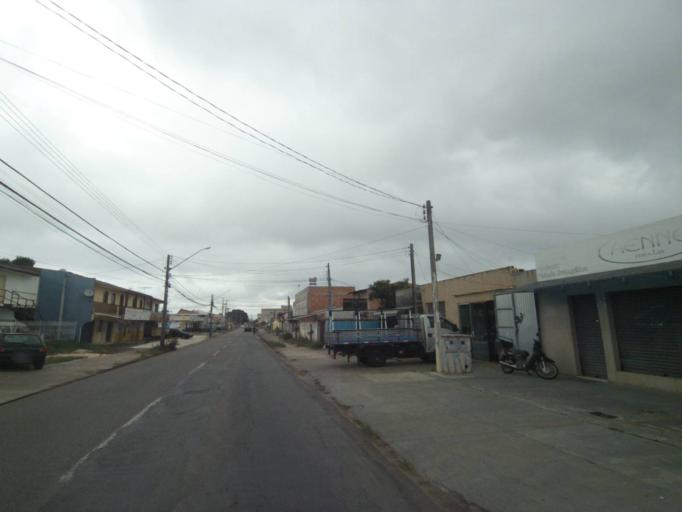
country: BR
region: Parana
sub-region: Pinhais
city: Pinhais
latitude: -25.4449
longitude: -49.1798
